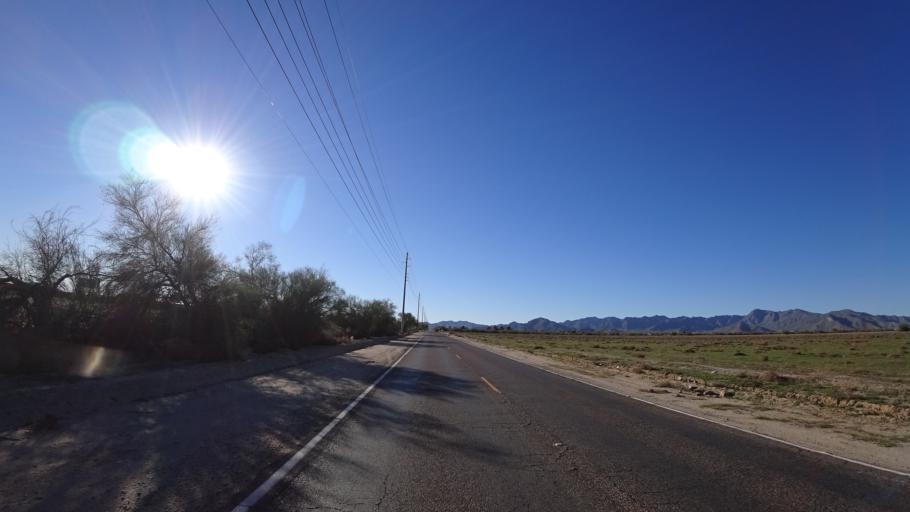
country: US
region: Arizona
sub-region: Maricopa County
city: Citrus Park
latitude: 33.4646
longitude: -112.4641
